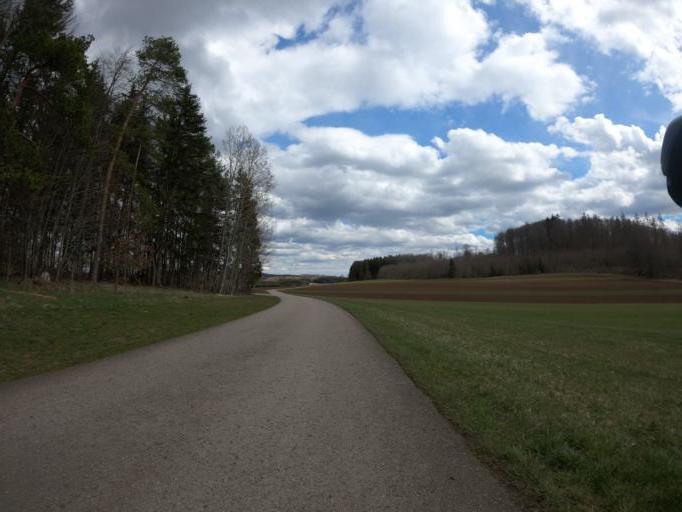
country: DE
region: Baden-Wuerttemberg
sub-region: Tuebingen Region
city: Trochtelfingen
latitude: 48.3807
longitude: 9.1968
